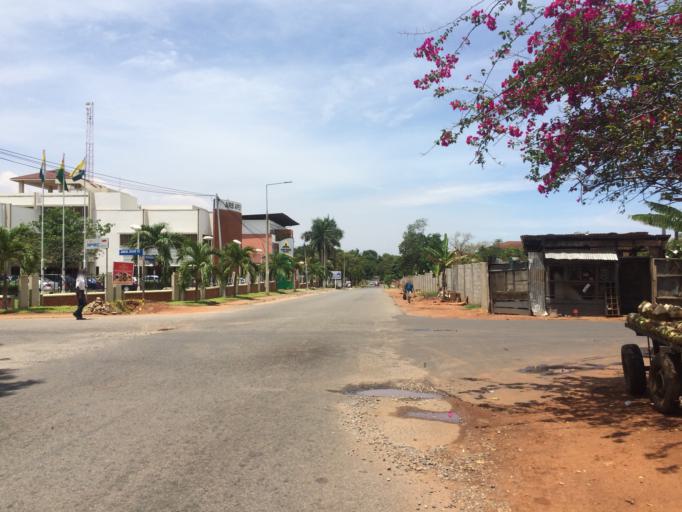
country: GH
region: Greater Accra
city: Accra
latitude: 5.5602
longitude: -0.1945
